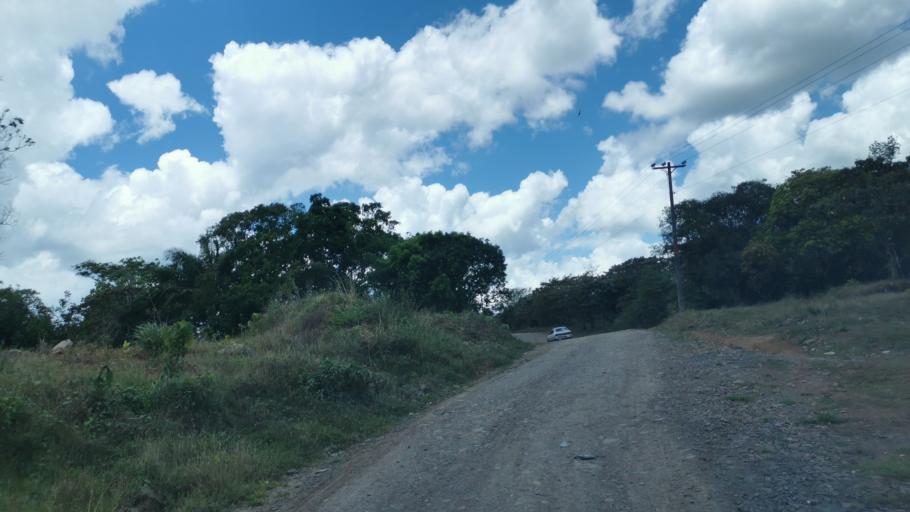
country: NI
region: Atlantico Sur
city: Rama
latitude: 12.3785
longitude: -84.2973
